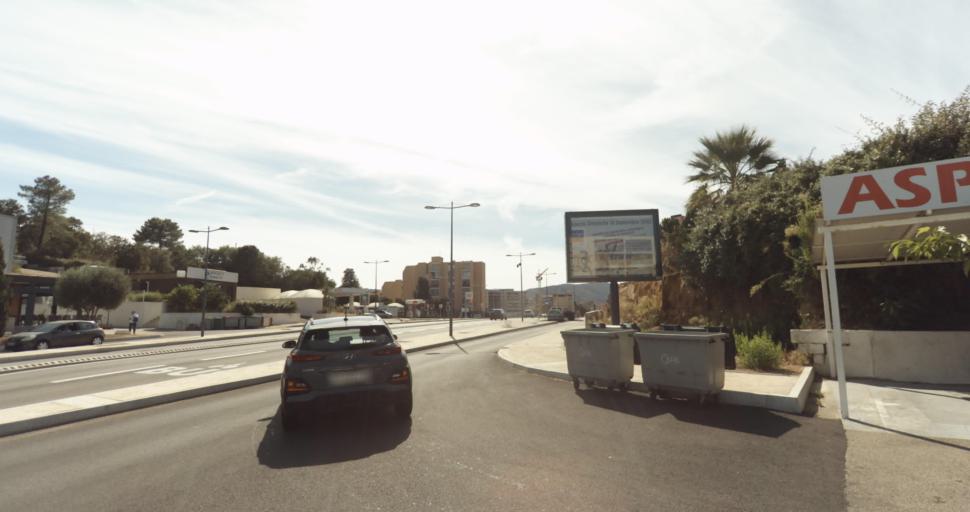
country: FR
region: Corsica
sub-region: Departement de la Corse-du-Sud
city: Ajaccio
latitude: 41.9444
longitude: 8.7556
